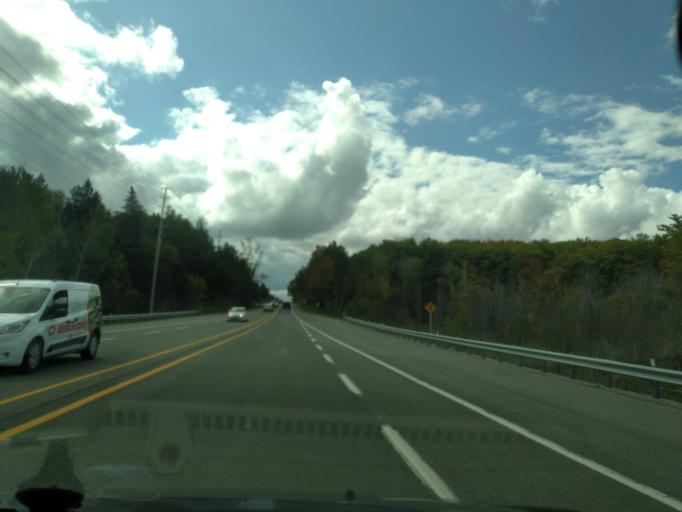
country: CA
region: Ontario
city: Innisfil
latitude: 44.2903
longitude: -79.6567
